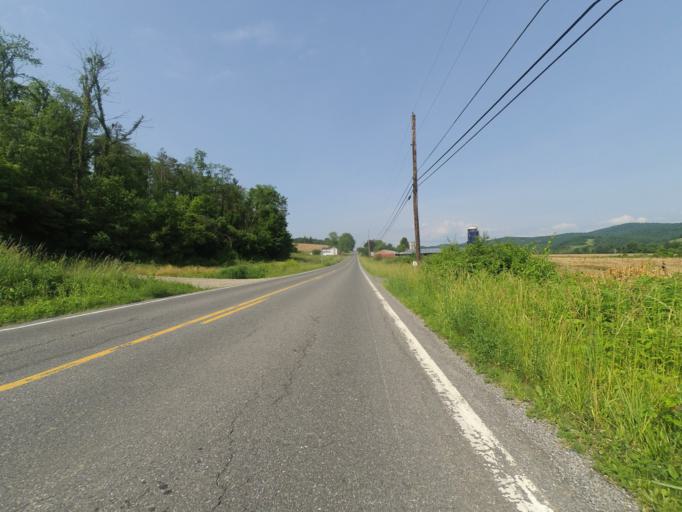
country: US
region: Pennsylvania
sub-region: Centre County
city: Milesburg
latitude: 40.9705
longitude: -77.7307
